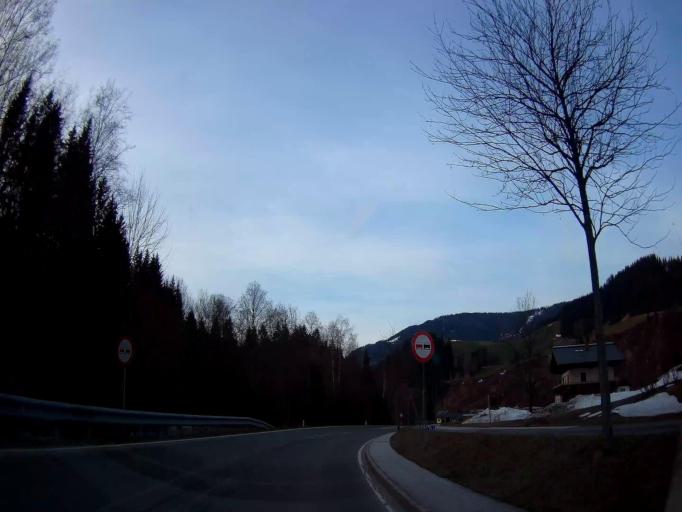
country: AT
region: Salzburg
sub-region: Politischer Bezirk Hallein
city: Abtenau
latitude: 47.5299
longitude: 13.4250
